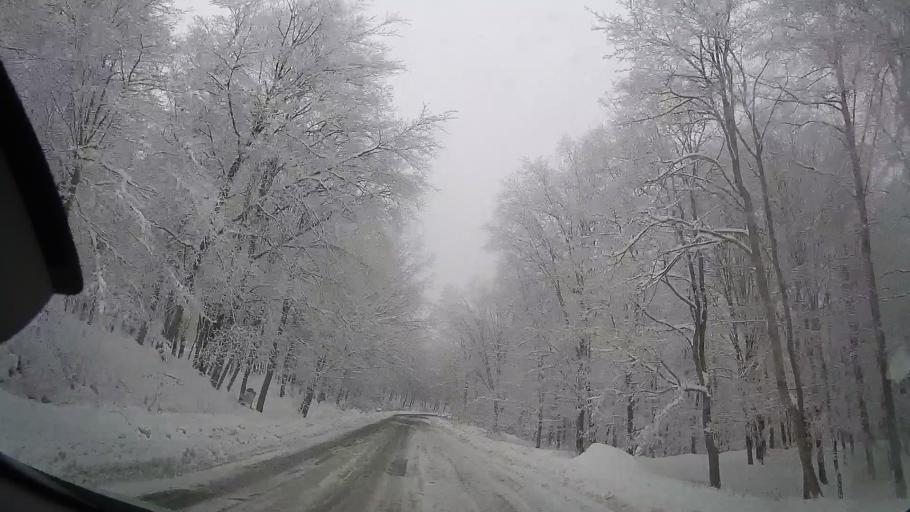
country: RO
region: Neamt
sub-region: Comuna Valea Ursului
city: Valea Ursului
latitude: 46.8383
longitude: 27.0692
